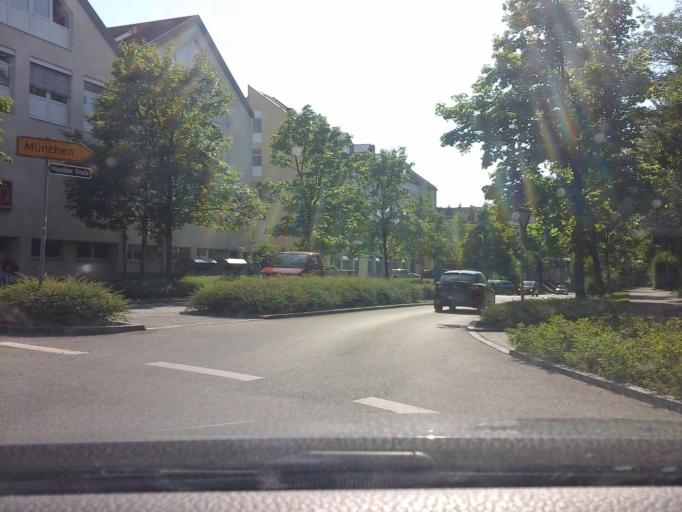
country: DE
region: Bavaria
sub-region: Upper Bavaria
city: Unterhaching
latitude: 48.0664
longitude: 11.6143
